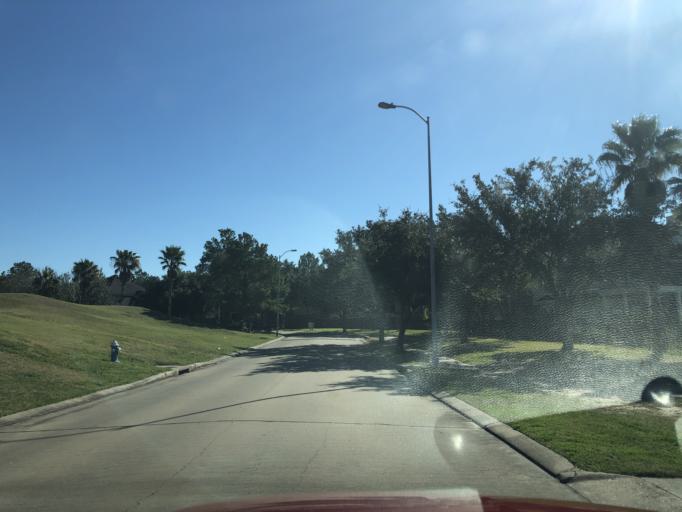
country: US
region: Texas
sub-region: Harris County
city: Oak Cliff Place
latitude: 29.9368
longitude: -95.6643
